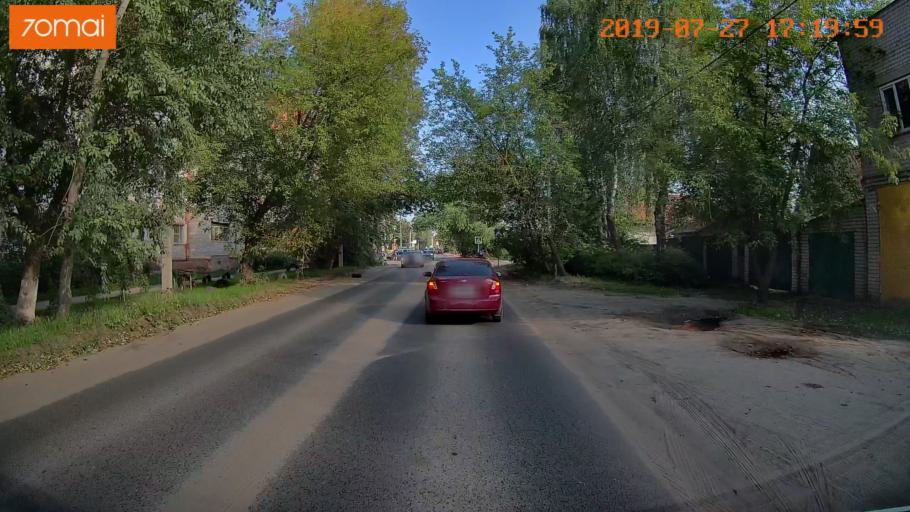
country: RU
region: Ivanovo
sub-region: Gorod Ivanovo
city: Ivanovo
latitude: 57.0318
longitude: 40.9206
